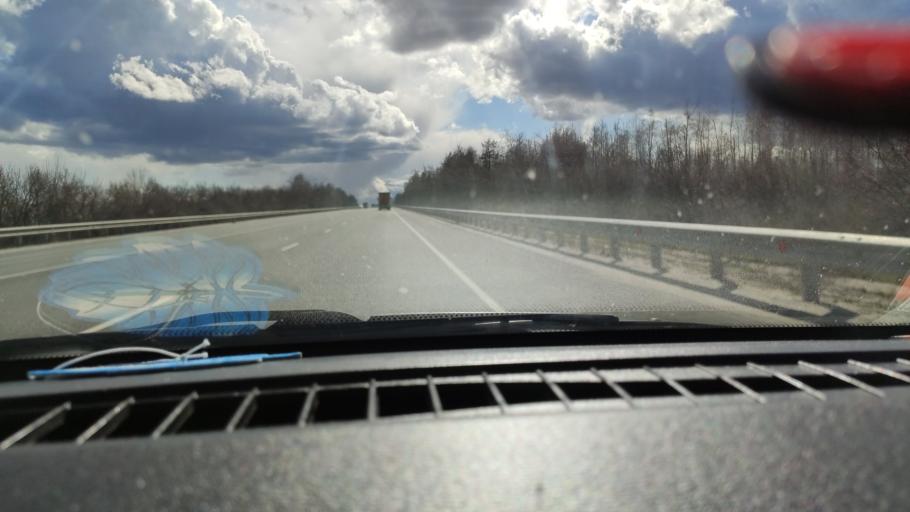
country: RU
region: Saratov
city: Khvalynsk
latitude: 52.5626
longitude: 48.0910
